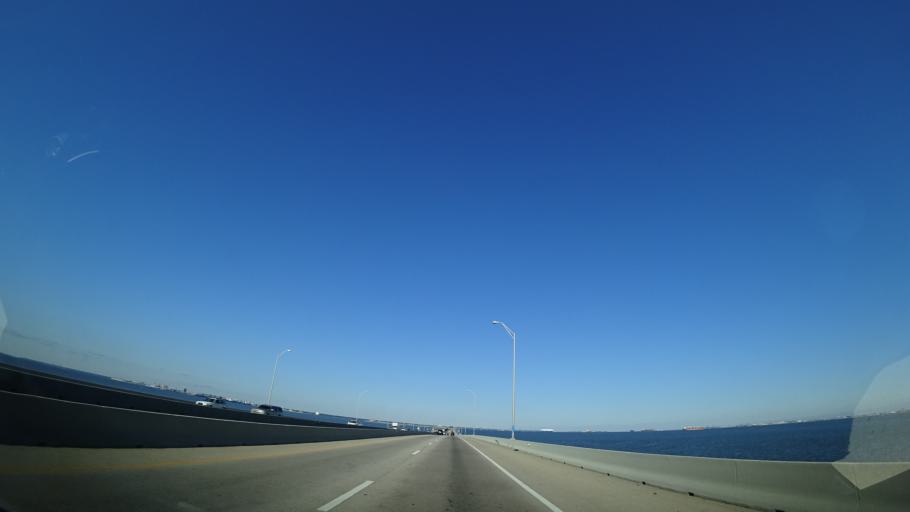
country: US
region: Virginia
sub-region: City of Newport News
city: Newport News
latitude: 36.9201
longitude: -76.4128
